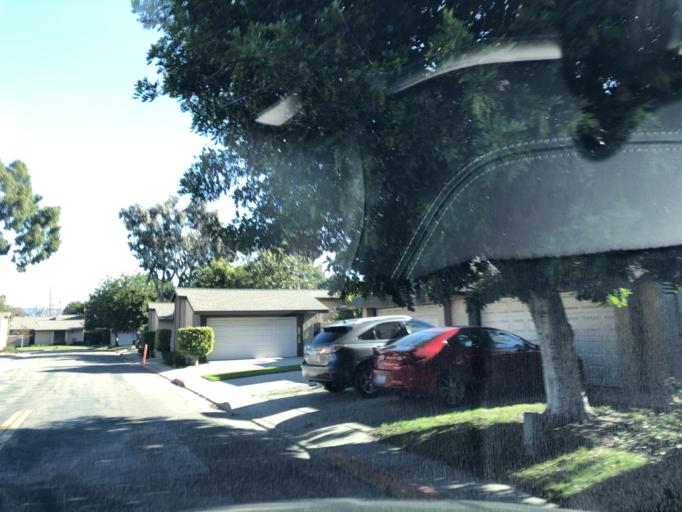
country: US
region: California
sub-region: Orange County
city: Orange
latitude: 33.7707
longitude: -117.8381
